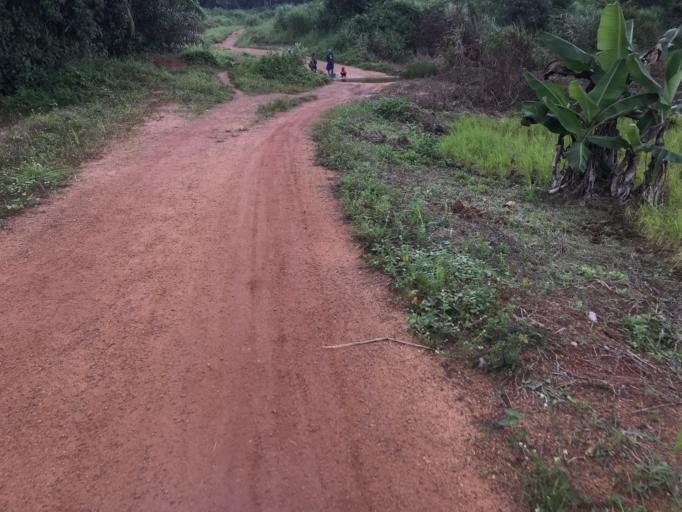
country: GN
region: Nzerekore
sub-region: Prefecture de Guekedou
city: Gueckedou
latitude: 8.4737
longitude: -10.2861
